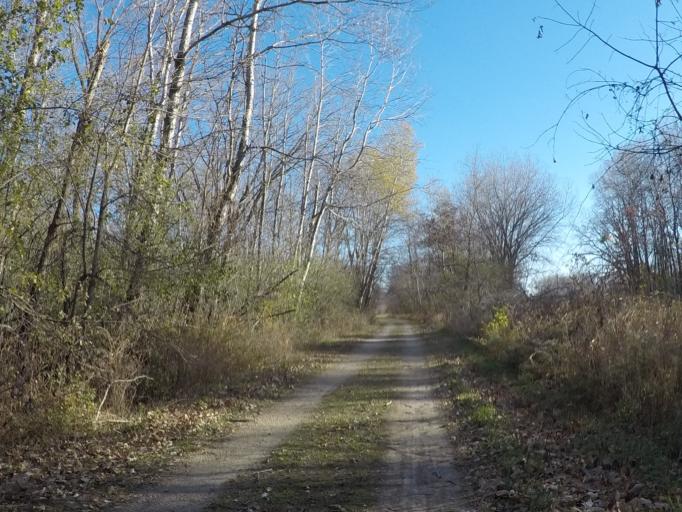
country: US
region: Wisconsin
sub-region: Jefferson County
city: Cambridge
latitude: 43.0444
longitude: -89.0209
